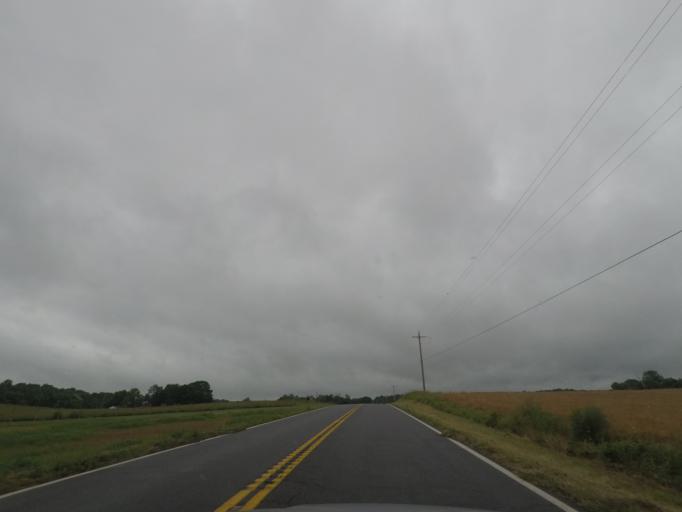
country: US
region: Virginia
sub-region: Culpeper County
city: Merrimac
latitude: 38.4082
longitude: -78.0596
